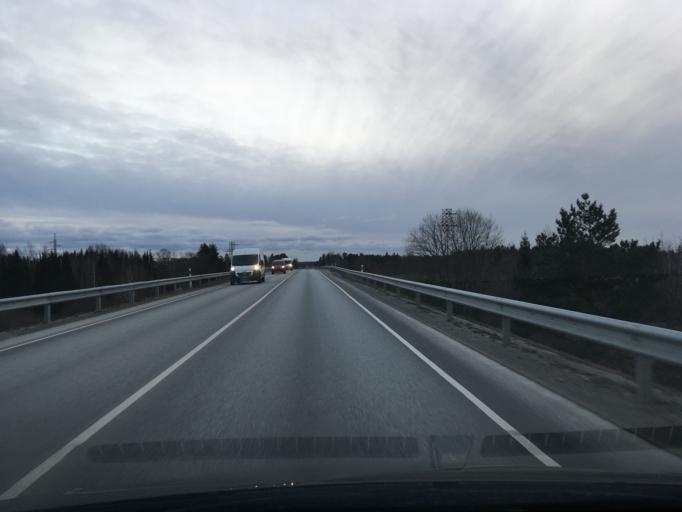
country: EE
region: Harju
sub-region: Nissi vald
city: Riisipere
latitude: 59.1282
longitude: 24.3156
